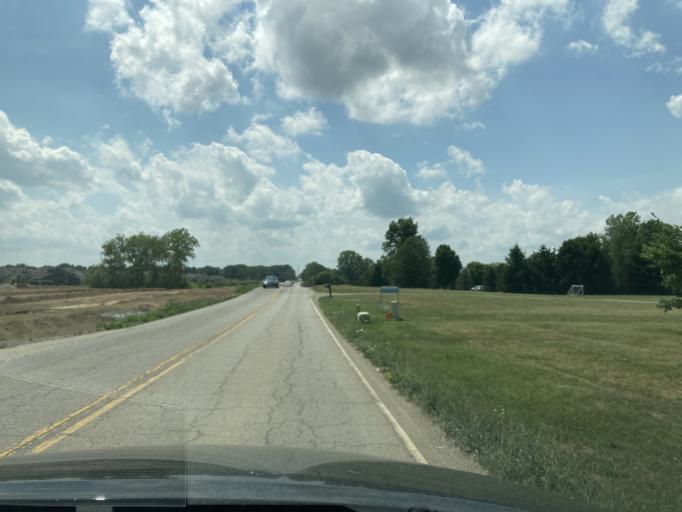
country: US
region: Indiana
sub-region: Boone County
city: Zionsville
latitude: 39.9988
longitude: -86.2303
